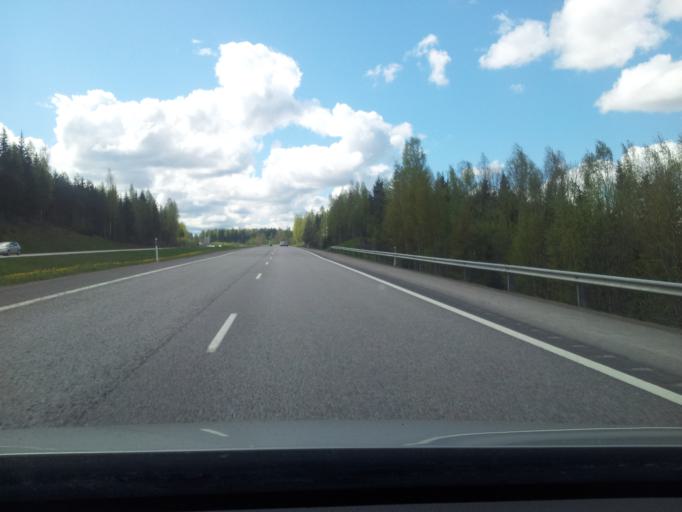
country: FI
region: Uusimaa
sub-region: Loviisa
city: Perna
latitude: 60.4807
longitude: 25.8758
